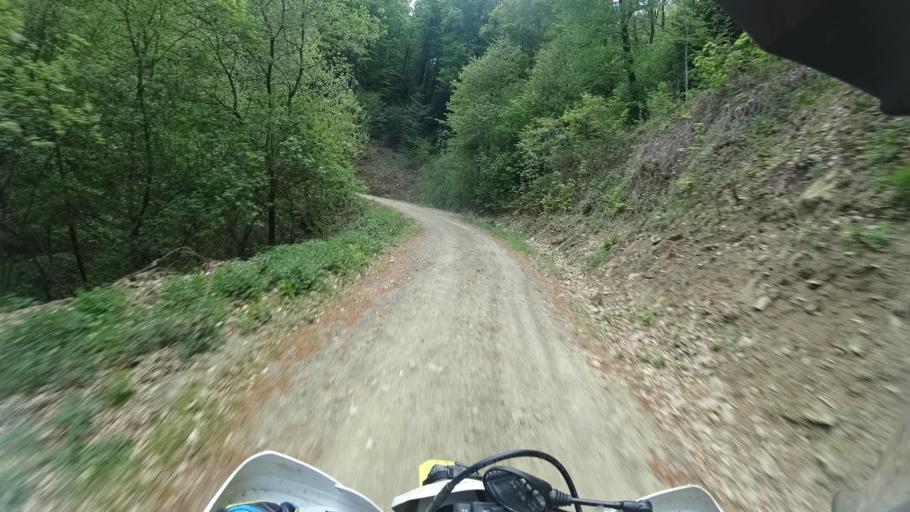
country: HR
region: Grad Zagreb
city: Kasina
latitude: 45.9237
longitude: 16.0325
